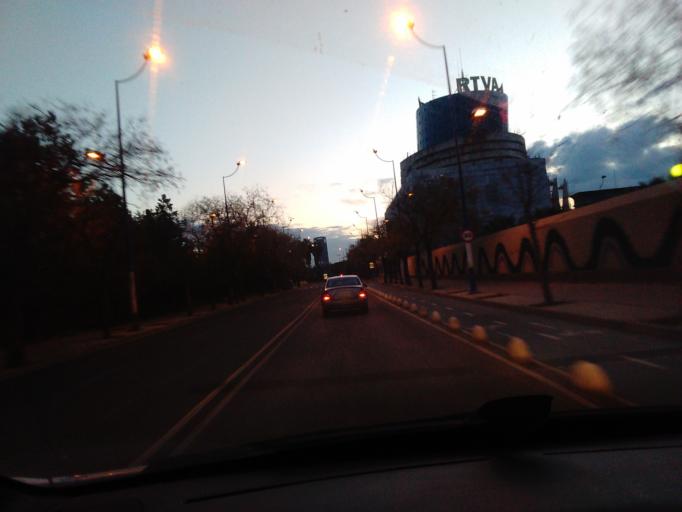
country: ES
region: Andalusia
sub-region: Provincia de Sevilla
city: Sevilla
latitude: 37.4069
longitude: -5.9977
